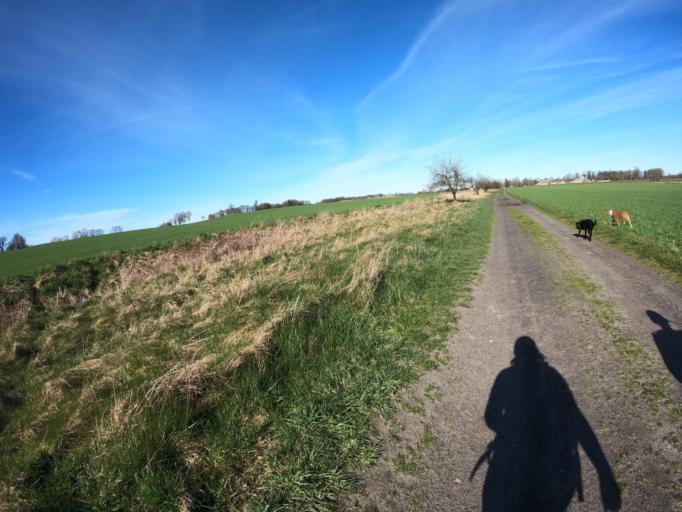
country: PL
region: West Pomeranian Voivodeship
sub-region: Powiat gryficki
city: Brojce
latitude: 53.9244
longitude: 15.3174
